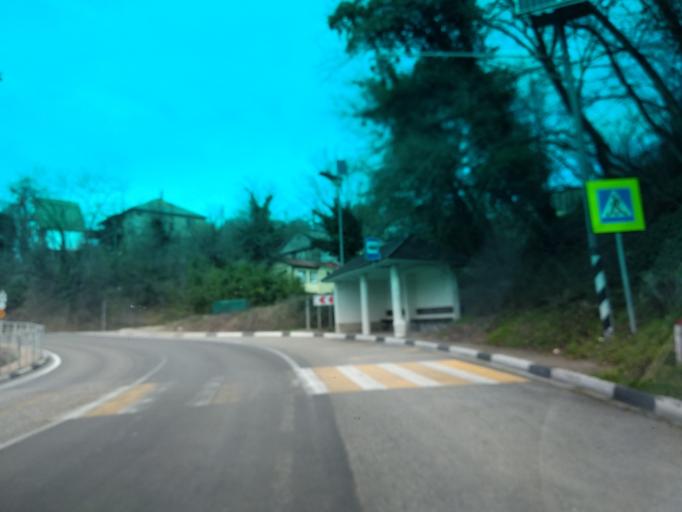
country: RU
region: Krasnodarskiy
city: Shepsi
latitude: 44.0416
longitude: 39.1423
